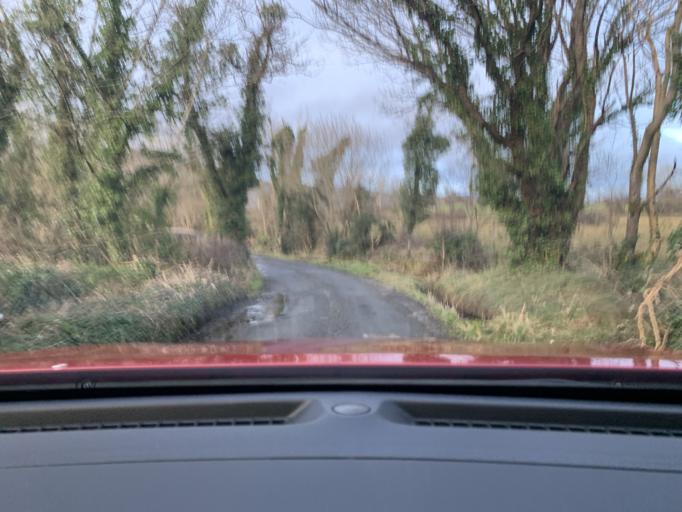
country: IE
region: Connaught
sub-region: Sligo
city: Sligo
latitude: 54.3162
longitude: -8.4480
